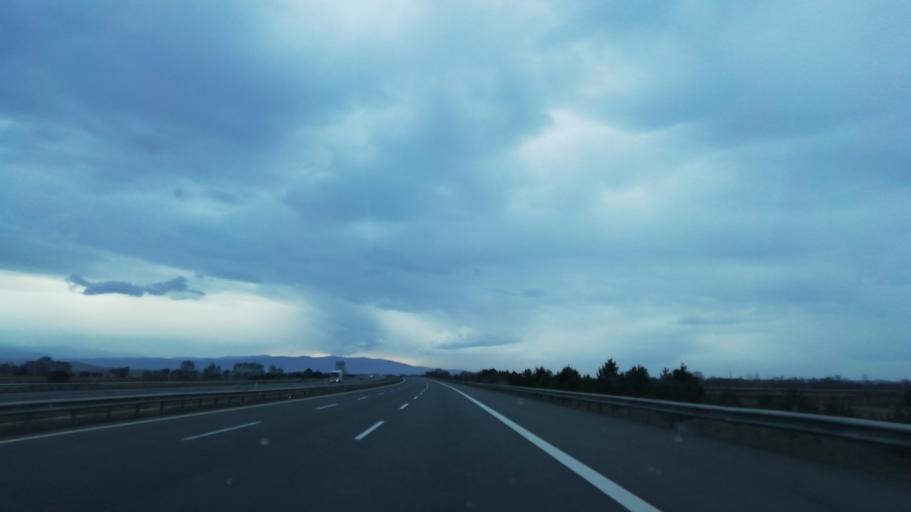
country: TR
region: Bolu
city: Gerede
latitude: 40.7404
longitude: 32.1681
